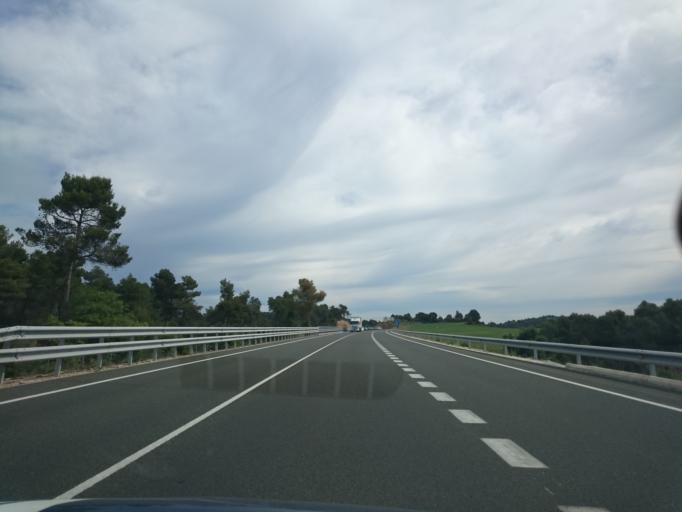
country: ES
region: Catalonia
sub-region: Provincia de Barcelona
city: Castelloli
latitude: 41.6267
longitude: 1.6872
